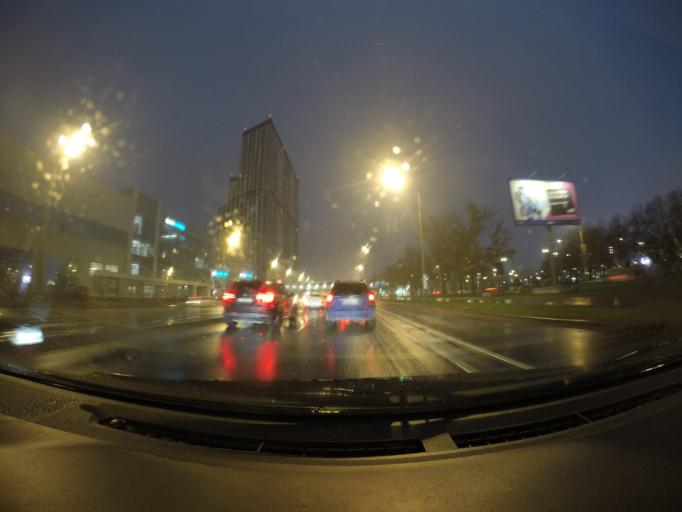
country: RU
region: Moskovskaya
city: Kozhukhovo
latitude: 55.6926
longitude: 37.6662
